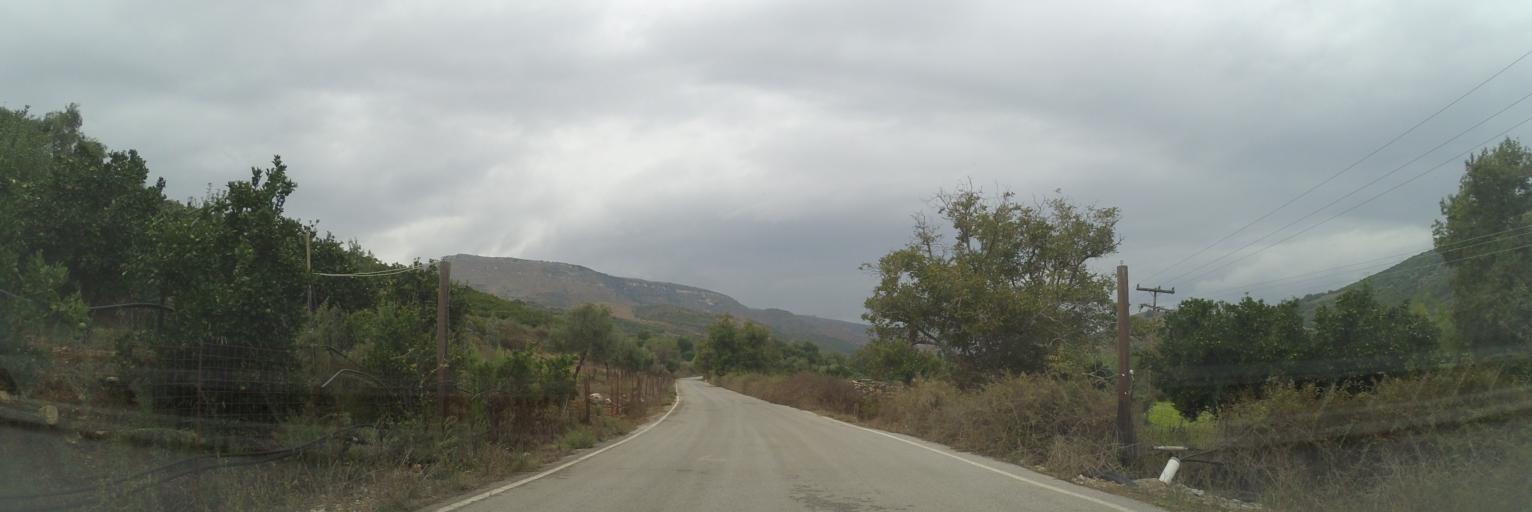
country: GR
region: Crete
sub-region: Nomos Rethymnis
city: Agia Foteini
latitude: 35.2877
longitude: 24.5651
